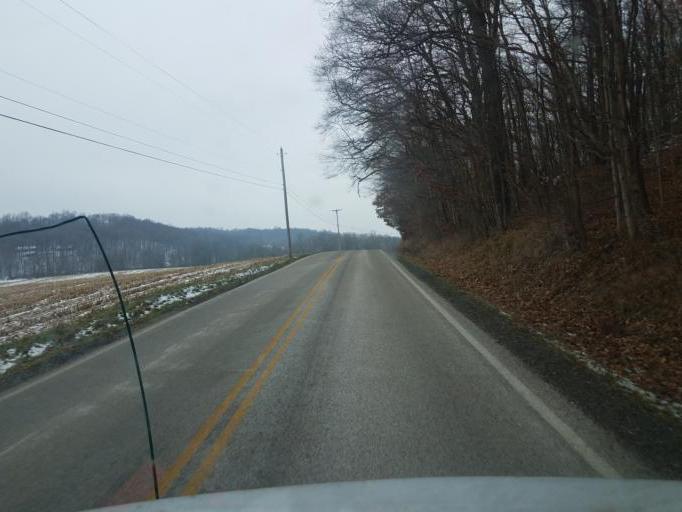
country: US
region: Ohio
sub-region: Sandusky County
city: Bellville
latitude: 40.6599
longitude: -82.4081
